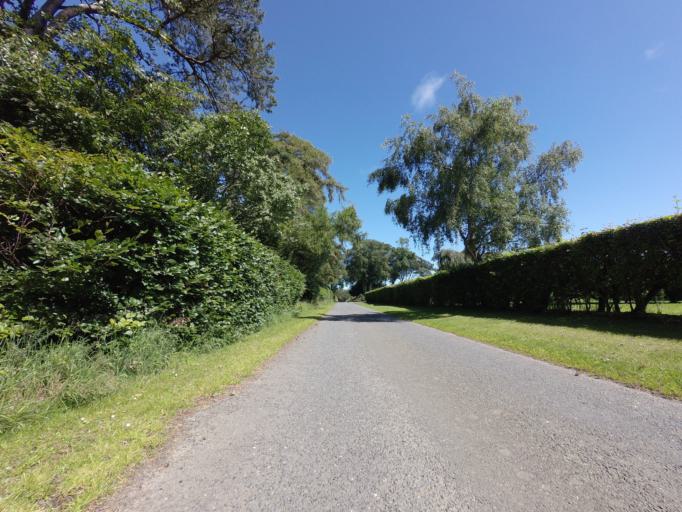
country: GB
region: Scotland
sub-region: Aberdeenshire
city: Macduff
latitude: 57.6236
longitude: -2.4955
